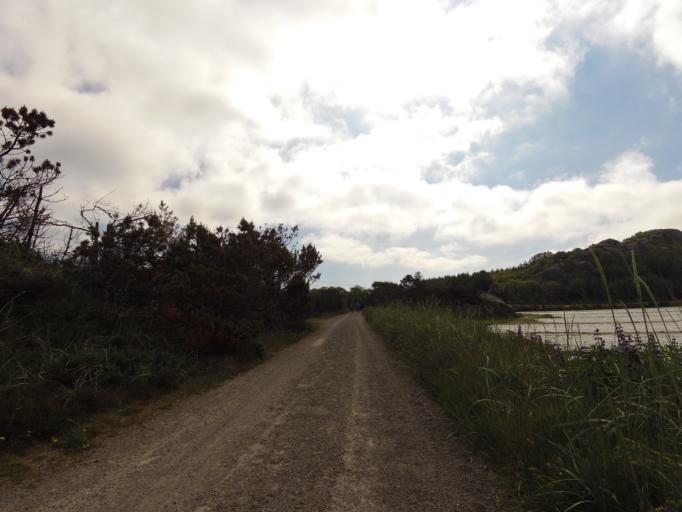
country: NO
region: Rogaland
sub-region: Ha
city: Vigrestad
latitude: 58.5261
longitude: 5.7859
